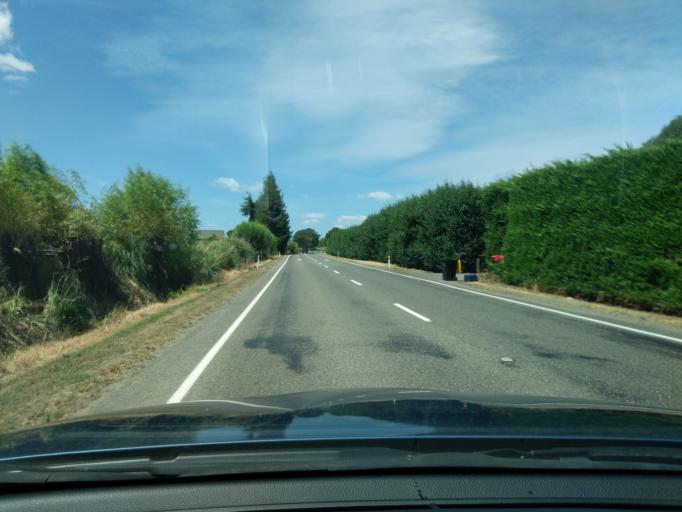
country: NZ
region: Tasman
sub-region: Tasman District
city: Motueka
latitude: -41.0596
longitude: 172.9715
